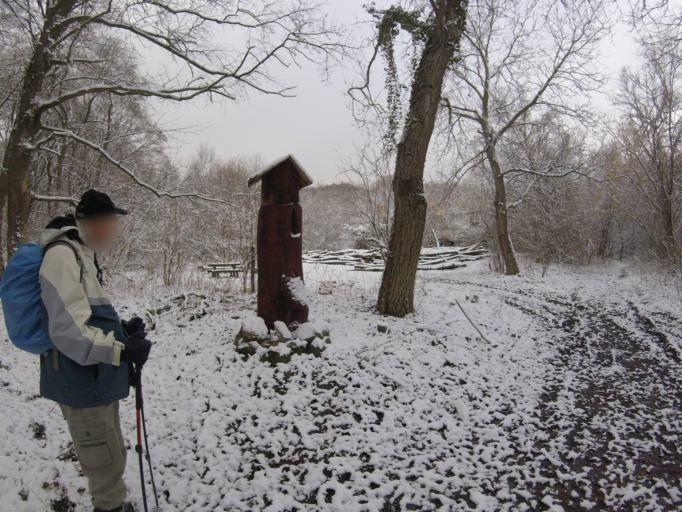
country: HU
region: Komarom-Esztergom
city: Esztergom
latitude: 47.7854
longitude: 18.7898
